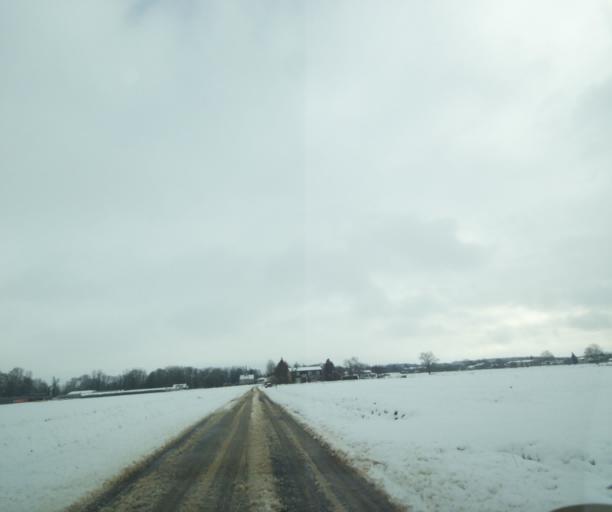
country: FR
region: Champagne-Ardenne
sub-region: Departement de la Haute-Marne
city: Montier-en-Der
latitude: 48.4969
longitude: 4.6939
